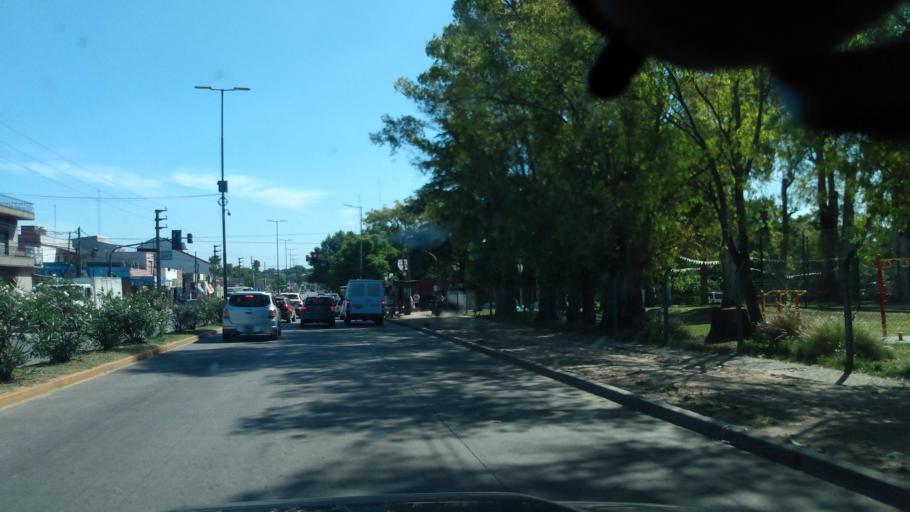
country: AR
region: Buenos Aires
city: Hurlingham
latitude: -34.5641
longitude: -58.7371
